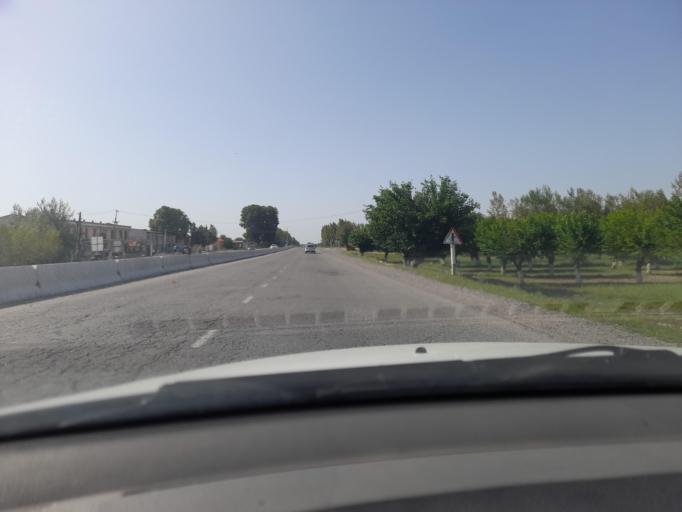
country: UZ
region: Samarqand
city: Daxbet
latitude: 39.8138
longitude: 66.8522
